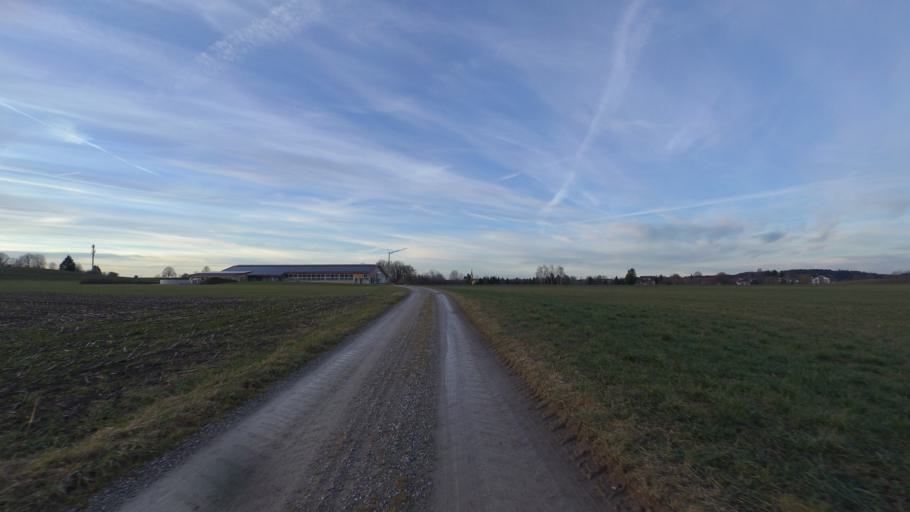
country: DE
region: Bavaria
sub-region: Upper Bavaria
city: Chieming
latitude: 47.8857
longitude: 12.5477
